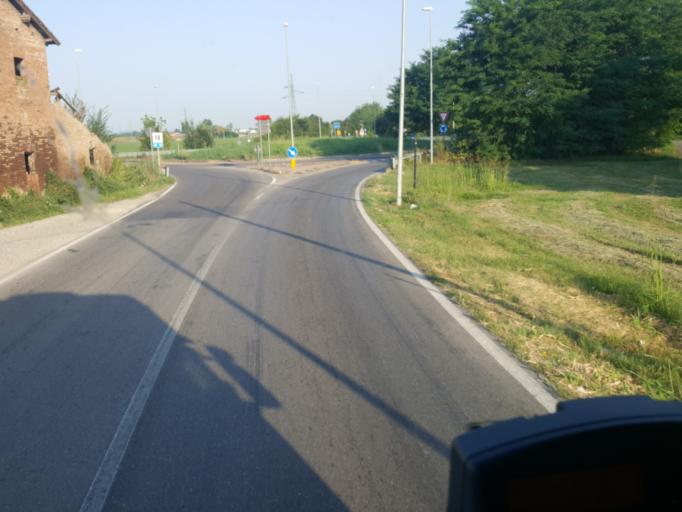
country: IT
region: Emilia-Romagna
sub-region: Provincia di Modena
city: San Vito
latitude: 44.5332
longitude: 10.9861
